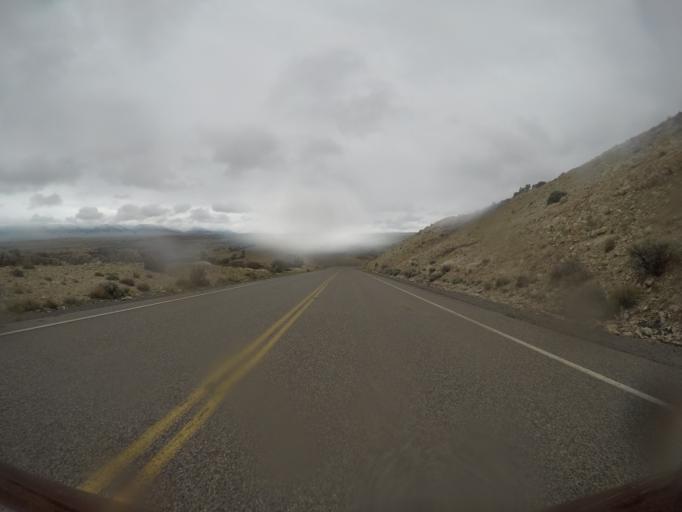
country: US
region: Wyoming
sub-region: Big Horn County
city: Lovell
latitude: 45.0491
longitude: -108.2545
